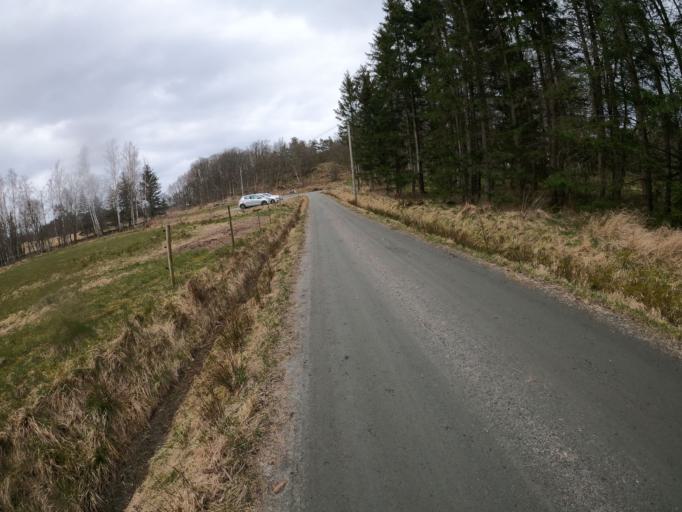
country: SE
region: Vaestra Goetaland
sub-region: Harryda Kommun
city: Molnlycke
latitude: 57.6265
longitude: 12.1077
